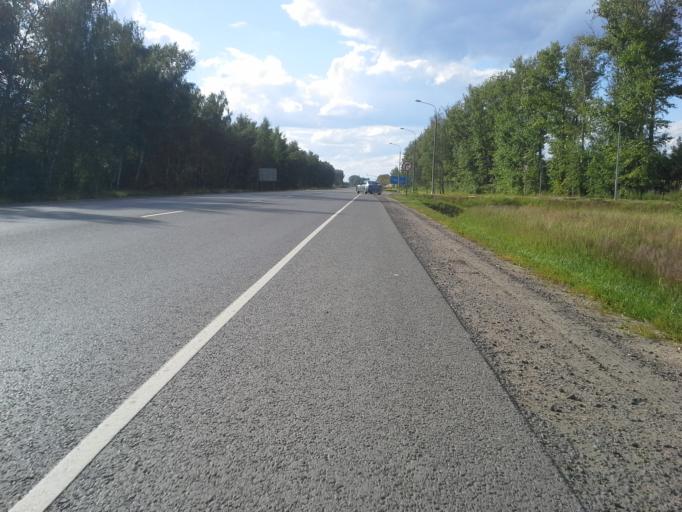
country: RU
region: Moskovskaya
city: L'vovskiy
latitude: 55.3442
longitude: 37.4573
